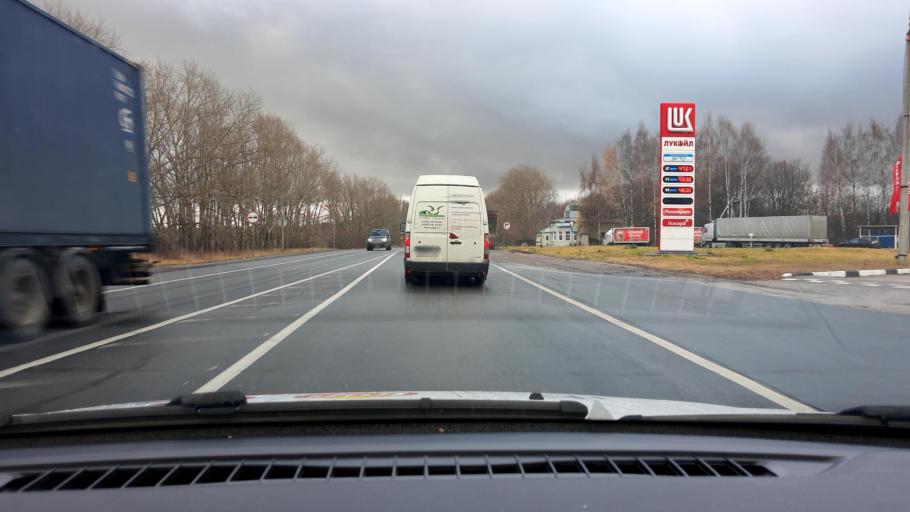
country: RU
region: Nizjnij Novgorod
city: Pamyat' Parizhskoy Kommuny
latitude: 56.0039
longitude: 44.6318
